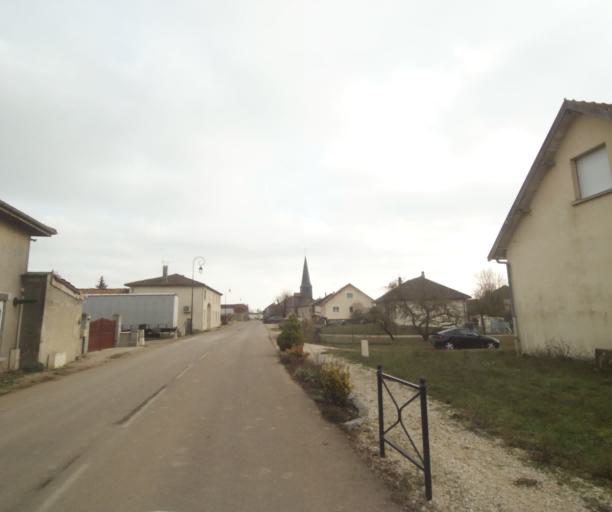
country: FR
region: Champagne-Ardenne
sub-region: Departement de la Haute-Marne
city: Villiers-en-Lieu
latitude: 48.6510
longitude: 4.8104
